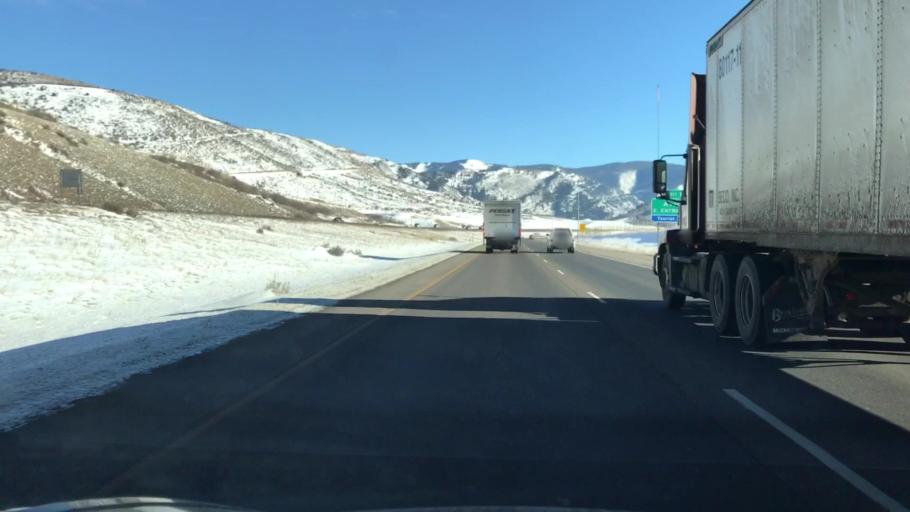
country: US
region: Colorado
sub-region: Eagle County
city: Avon
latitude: 39.6303
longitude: -106.5020
